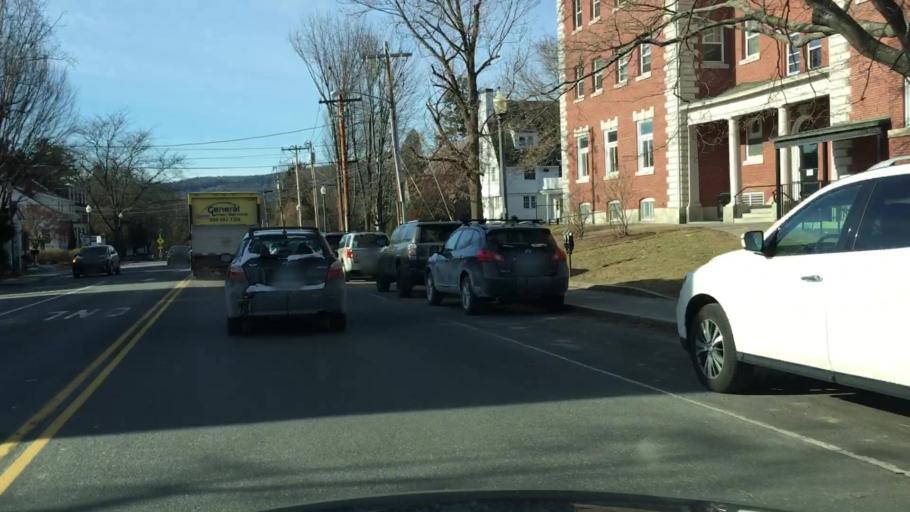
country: US
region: New Hampshire
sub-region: Grafton County
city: Hanover
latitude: 43.7025
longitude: -72.2896
